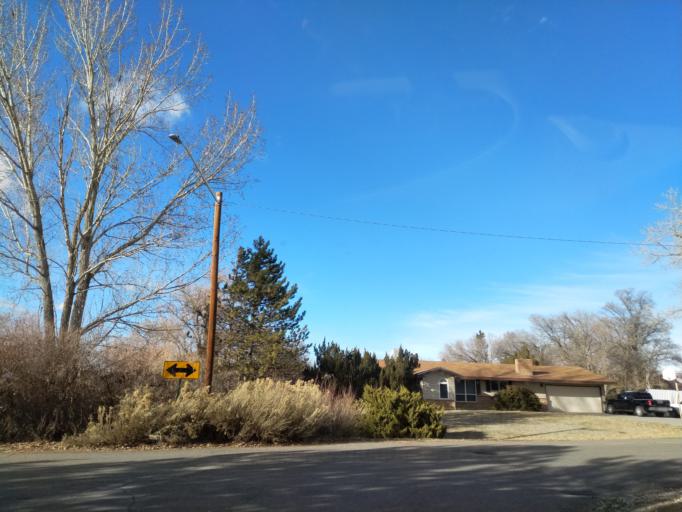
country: US
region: Colorado
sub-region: Mesa County
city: Grand Junction
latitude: 39.1098
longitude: -108.5648
